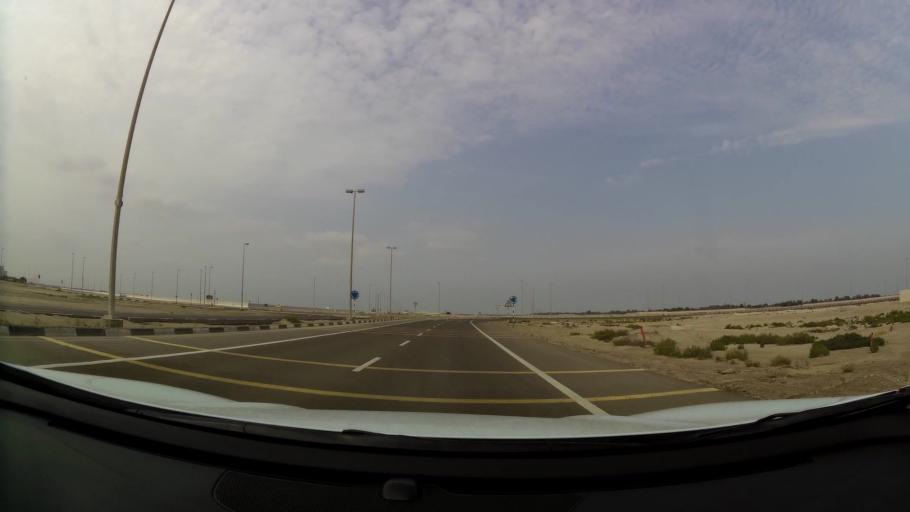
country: AE
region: Abu Dhabi
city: Abu Dhabi
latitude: 24.6394
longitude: 54.6653
